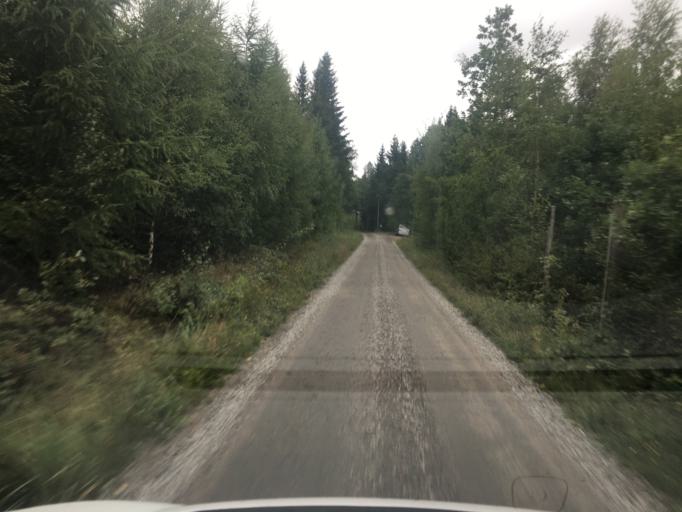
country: SE
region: Kronoberg
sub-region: Ljungby Kommun
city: Lagan
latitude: 56.9677
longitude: 14.0418
